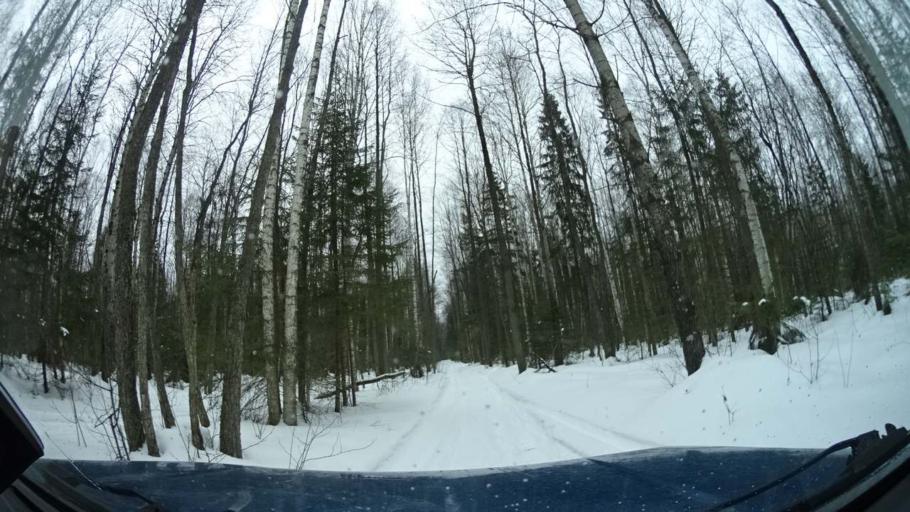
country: RU
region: Tverskaya
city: Gorodnya
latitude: 56.8065
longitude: 36.3756
